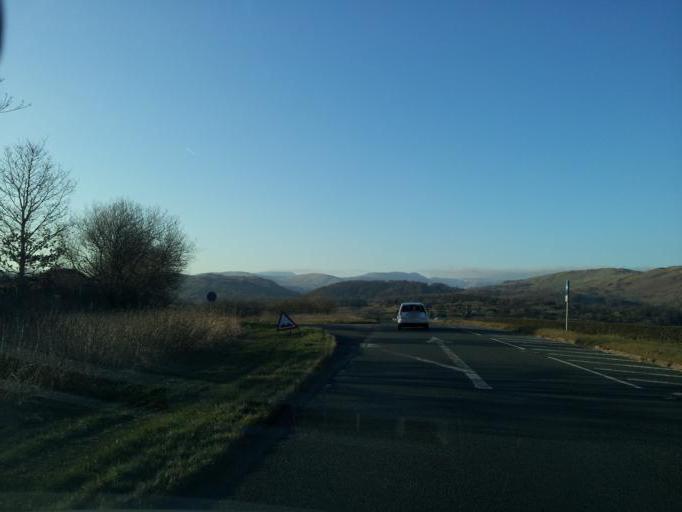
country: GB
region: England
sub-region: Cumbria
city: Kendal
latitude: 54.3573
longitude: -2.7857
